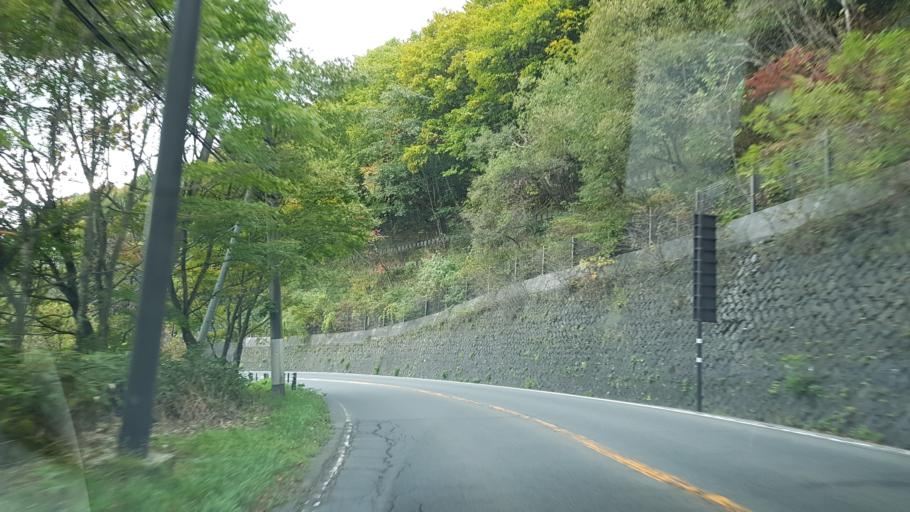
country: JP
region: Nagano
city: Nakano
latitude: 36.6095
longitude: 138.5832
